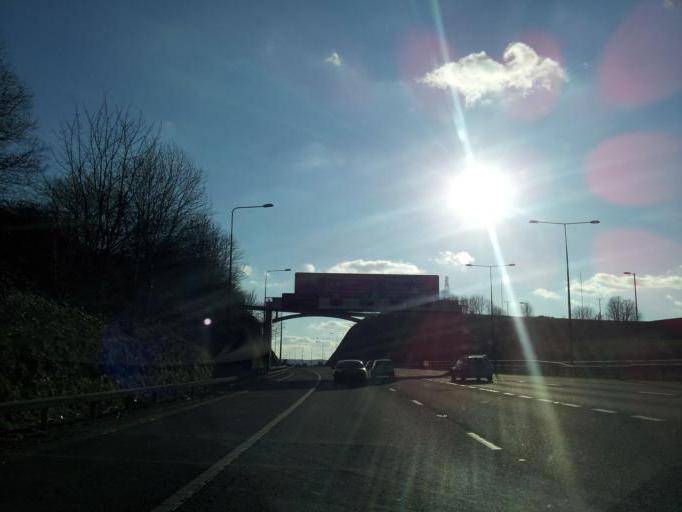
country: GB
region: England
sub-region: Devon
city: Exminster
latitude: 50.6842
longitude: -3.5089
